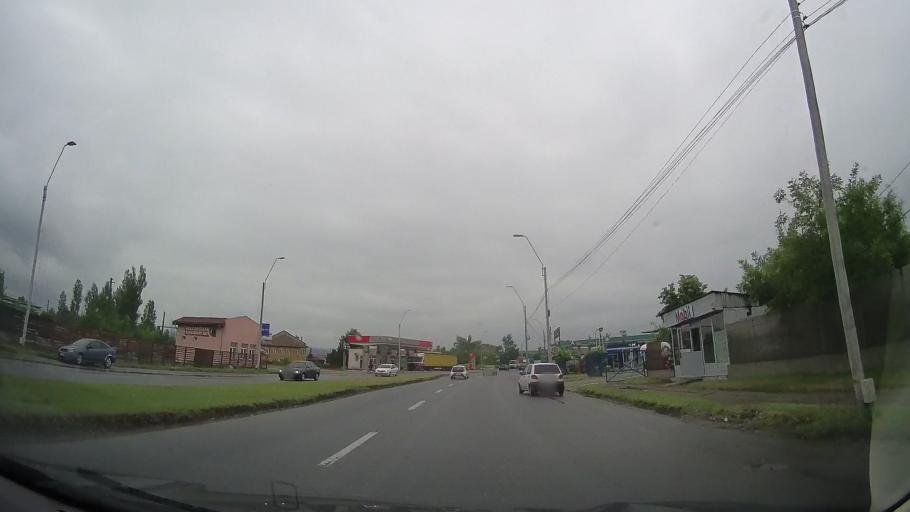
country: RO
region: Mehedinti
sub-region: Comuna Simian
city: Dudasu
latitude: 44.6317
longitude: 22.6841
